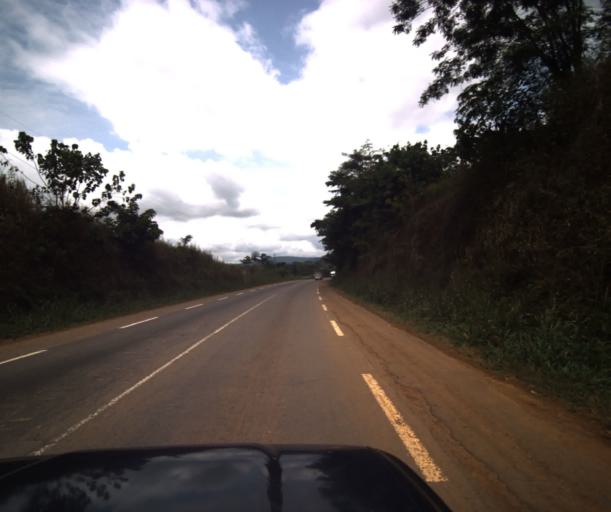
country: CM
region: Centre
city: Mbankomo
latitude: 3.7658
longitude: 11.0940
